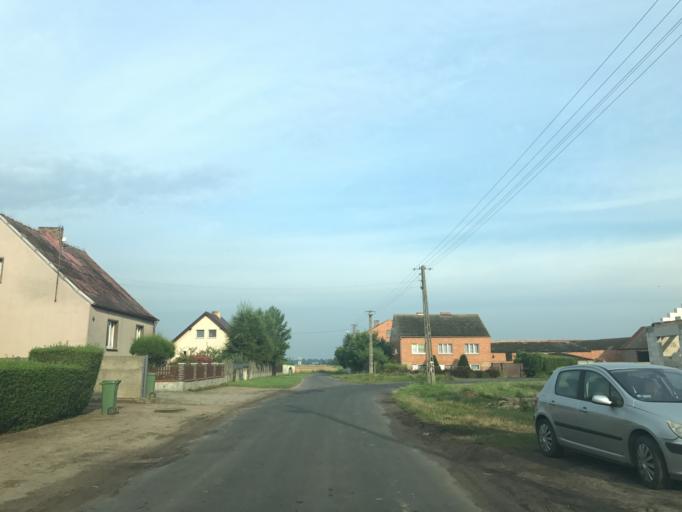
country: PL
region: Greater Poland Voivodeship
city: Miejska Gorka
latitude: 51.6327
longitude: 16.9613
